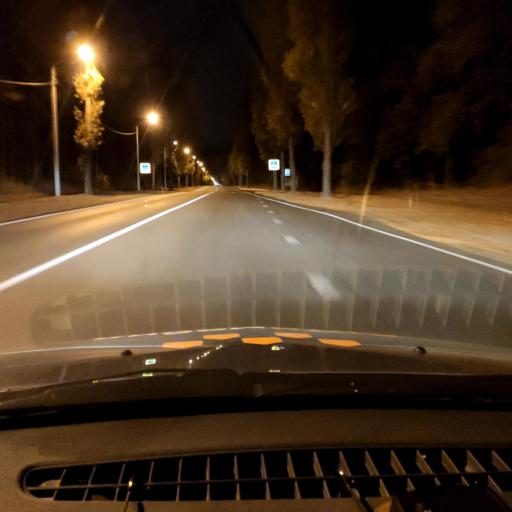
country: RU
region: Voronezj
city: Somovo
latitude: 51.6995
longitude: 39.3220
